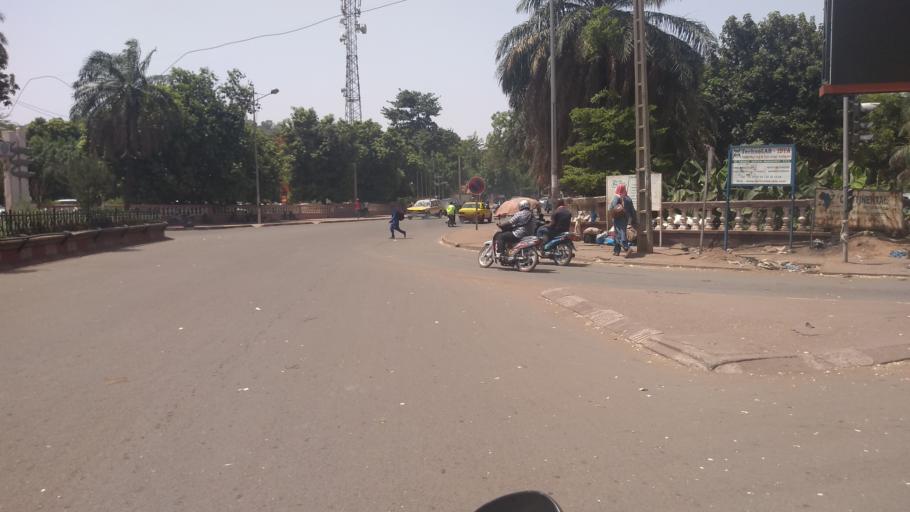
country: ML
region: Bamako
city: Bamako
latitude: 12.6469
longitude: -8.0012
